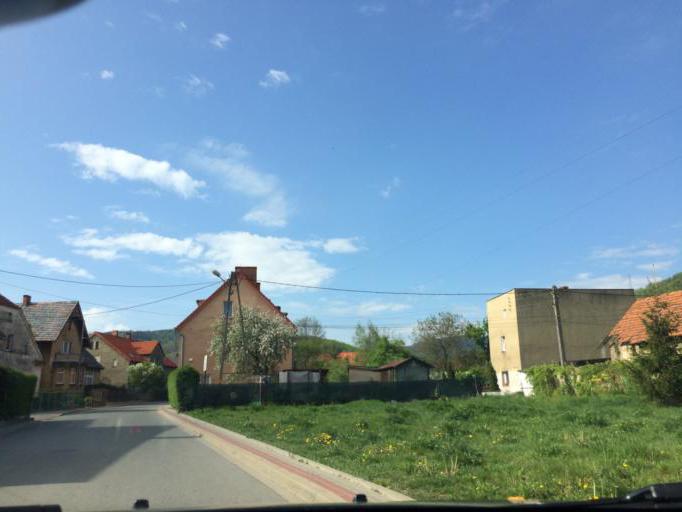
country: PL
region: Lower Silesian Voivodeship
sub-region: Powiat dzierzoniowski
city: Pieszyce
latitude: 50.7024
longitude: 16.5697
